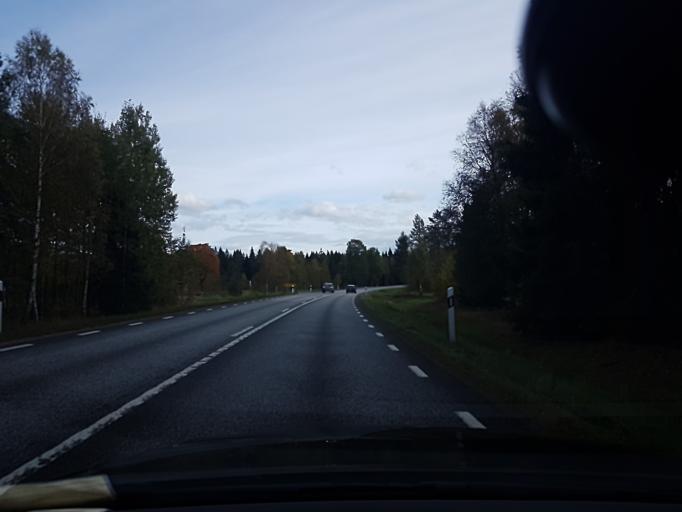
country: SE
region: Joenkoeping
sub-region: Varnamo Kommun
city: Bredaryd
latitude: 57.1774
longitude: 13.7589
